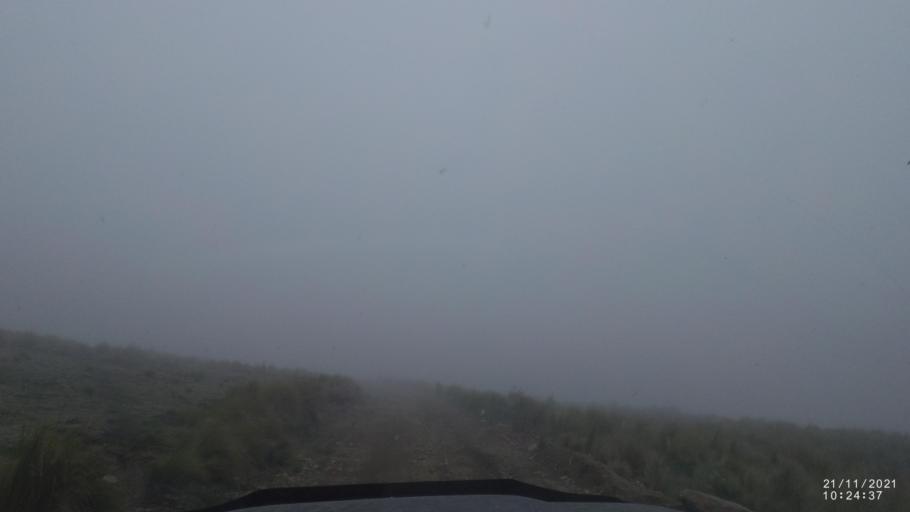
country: BO
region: Cochabamba
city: Cochabamba
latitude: -16.9784
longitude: -66.2635
